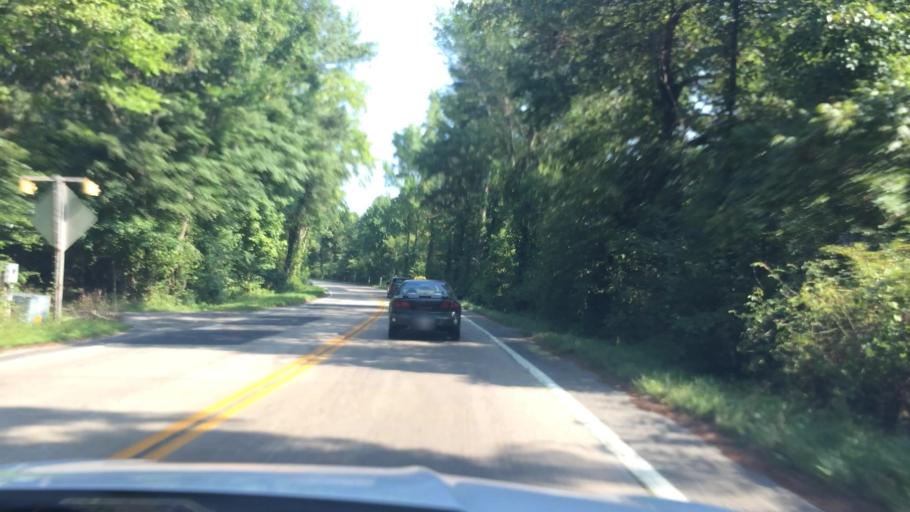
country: US
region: Virginia
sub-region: City of Williamsburg
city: Williamsburg
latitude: 37.3041
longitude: -76.6850
